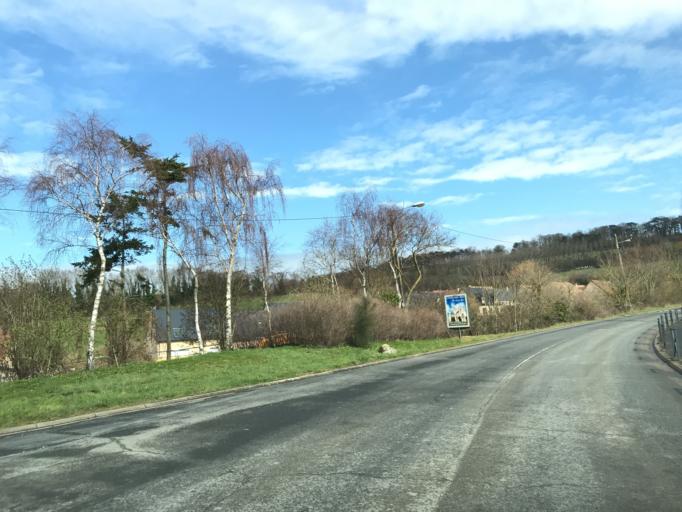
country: FR
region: Lower Normandy
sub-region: Departement du Calvados
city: Dives-sur-Mer
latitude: 49.2856
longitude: -0.0932
